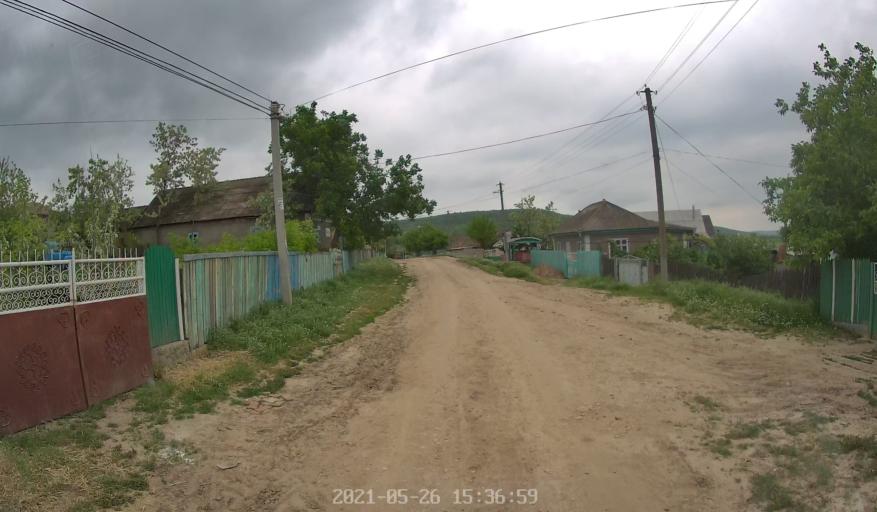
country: MD
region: Hincesti
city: Dancu
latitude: 46.6707
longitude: 28.3175
